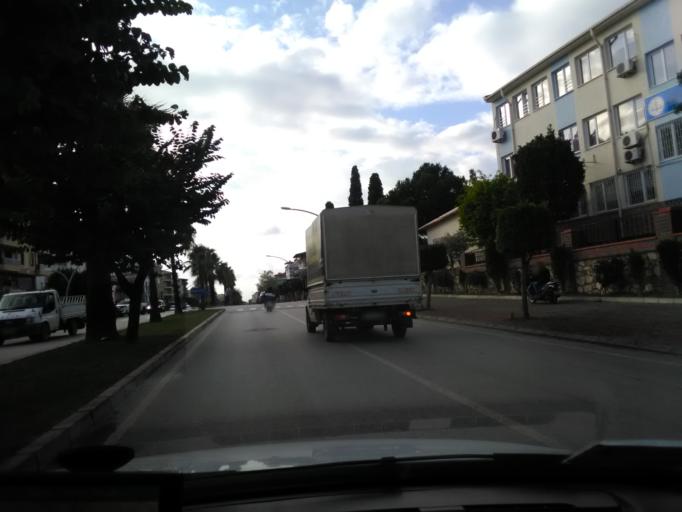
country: TR
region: Antalya
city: Gazipasa
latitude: 36.2682
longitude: 32.3128
